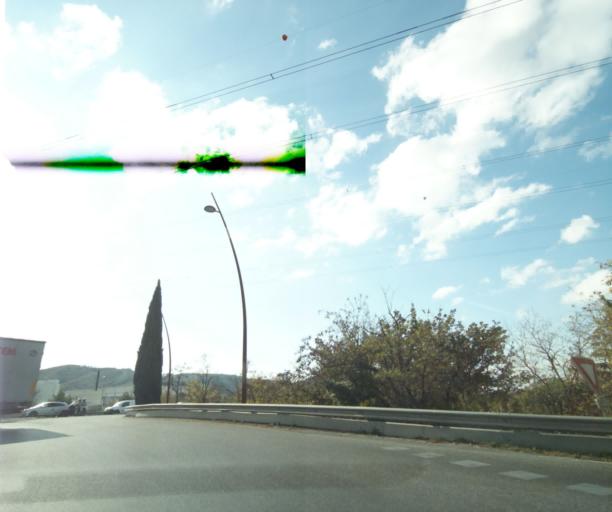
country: FR
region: Provence-Alpes-Cote d'Azur
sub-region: Departement des Bouches-du-Rhone
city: Les Pennes-Mirabeau
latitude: 43.4097
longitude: 5.3248
